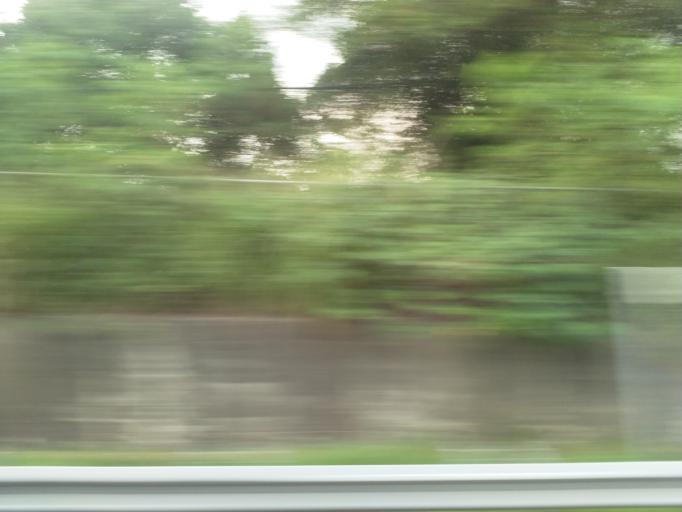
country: TW
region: Taiwan
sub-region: Pingtung
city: Pingtung
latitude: 22.7615
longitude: 120.3897
